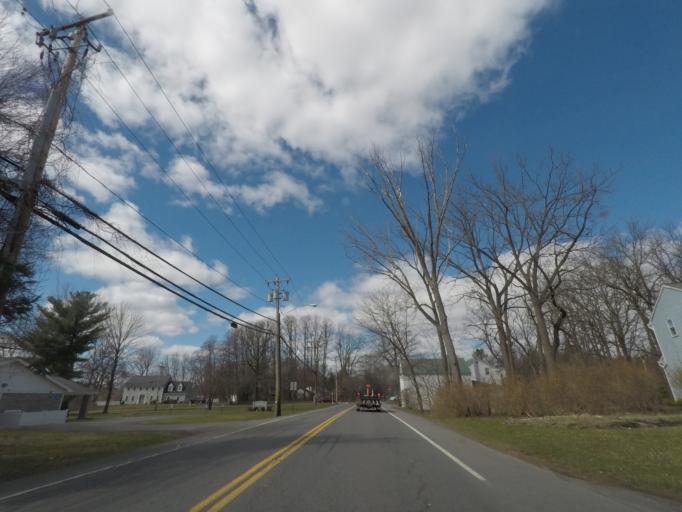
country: US
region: New York
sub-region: Albany County
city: Delmar
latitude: 42.5948
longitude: -73.8344
